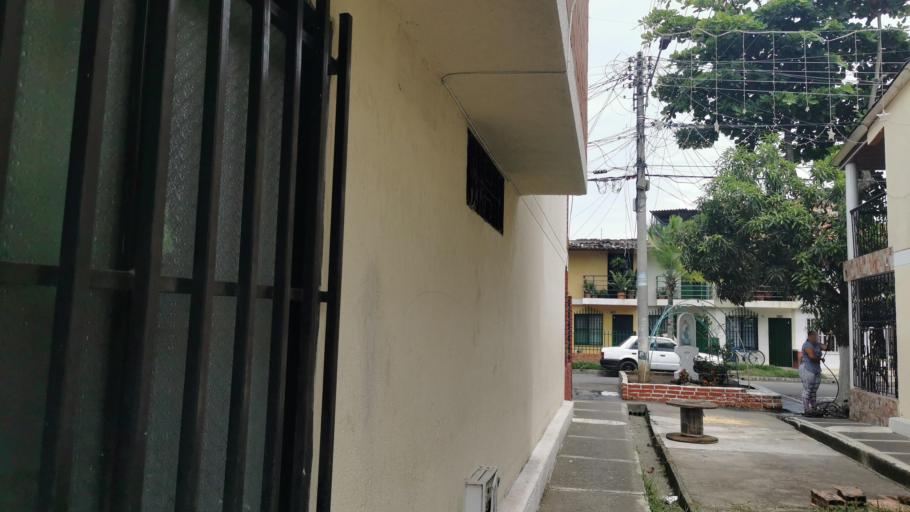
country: CO
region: Valle del Cauca
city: Jamundi
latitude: 3.2519
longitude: -76.5354
